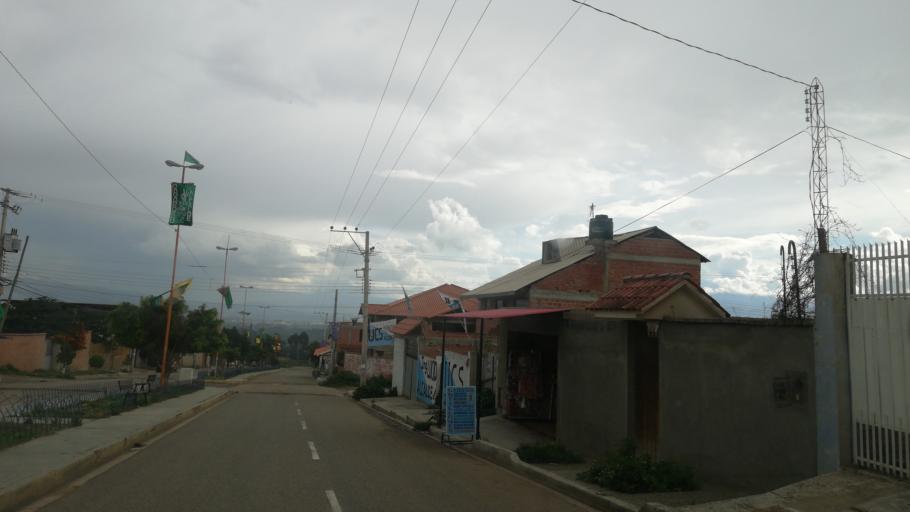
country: BO
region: Cochabamba
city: Cochabamba
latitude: -17.3349
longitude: -66.1980
